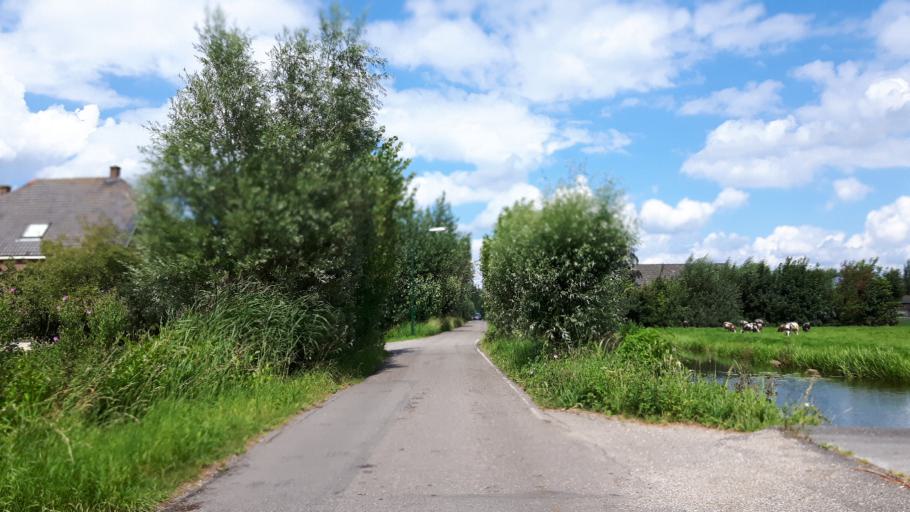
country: NL
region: Utrecht
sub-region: Stichtse Vecht
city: Breukelen
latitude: 52.1511
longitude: 4.9266
